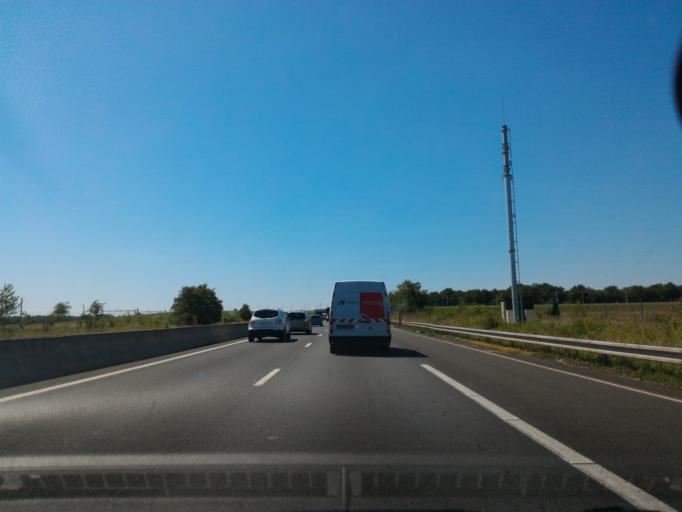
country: FR
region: Centre
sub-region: Departement d'Indre-et-Loire
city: Sorigny
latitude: 47.2304
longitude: 0.6585
